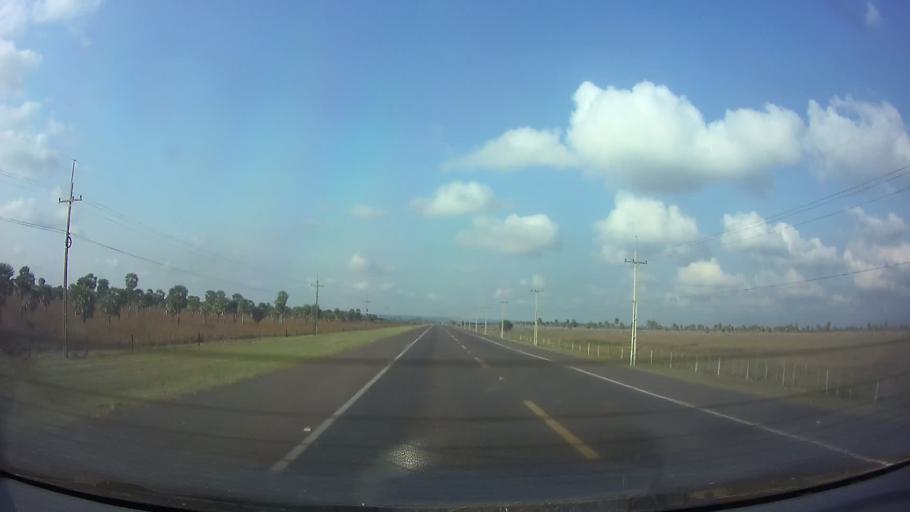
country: PY
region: Cordillera
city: Emboscada
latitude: -25.0803
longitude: -57.2756
